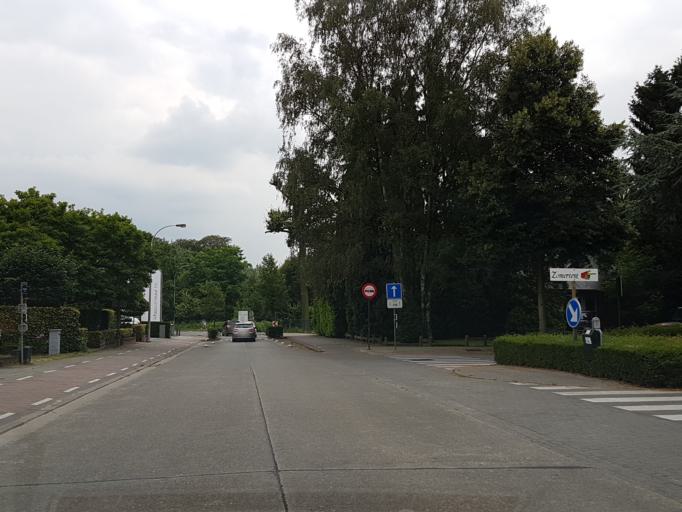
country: BE
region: Flanders
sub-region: Provincie Antwerpen
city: Schoten
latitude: 51.2459
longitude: 4.4974
